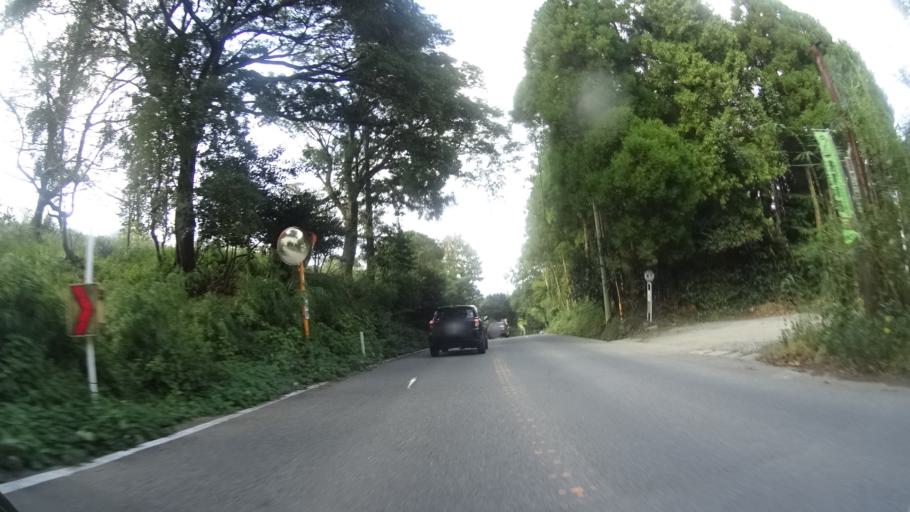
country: JP
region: Oita
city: Beppu
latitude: 33.2891
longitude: 131.4562
